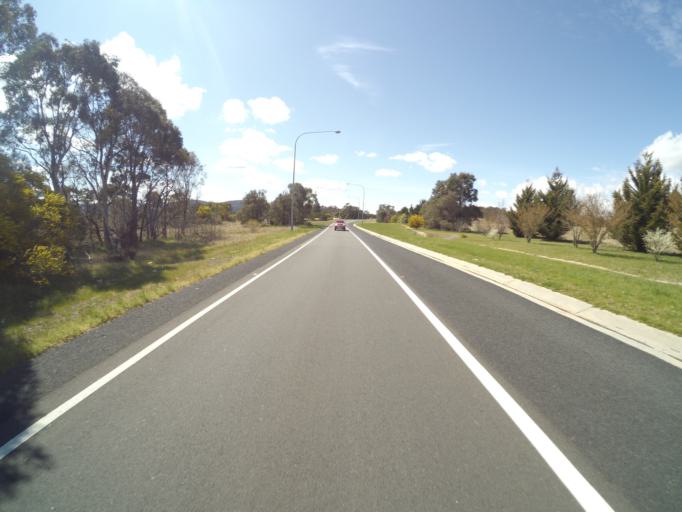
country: AU
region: New South Wales
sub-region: Goulburn Mulwaree
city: Goulburn
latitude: -34.7416
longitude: 149.7748
